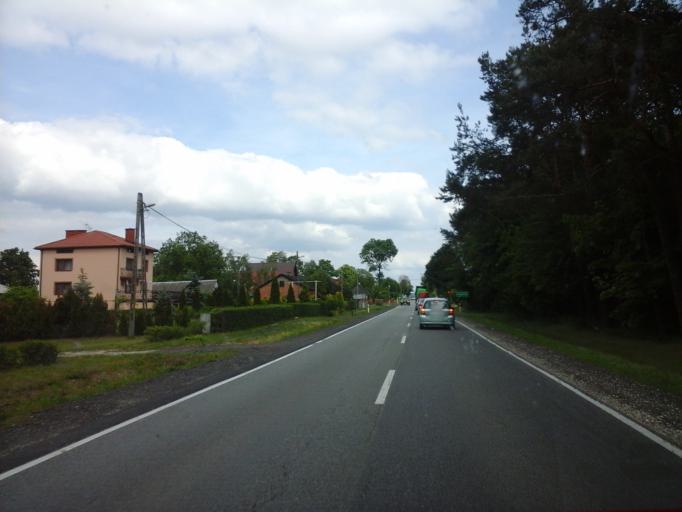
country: PL
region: Lodz Voivodeship
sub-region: Powiat opoczynski
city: Paradyz
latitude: 51.3093
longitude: 20.0952
